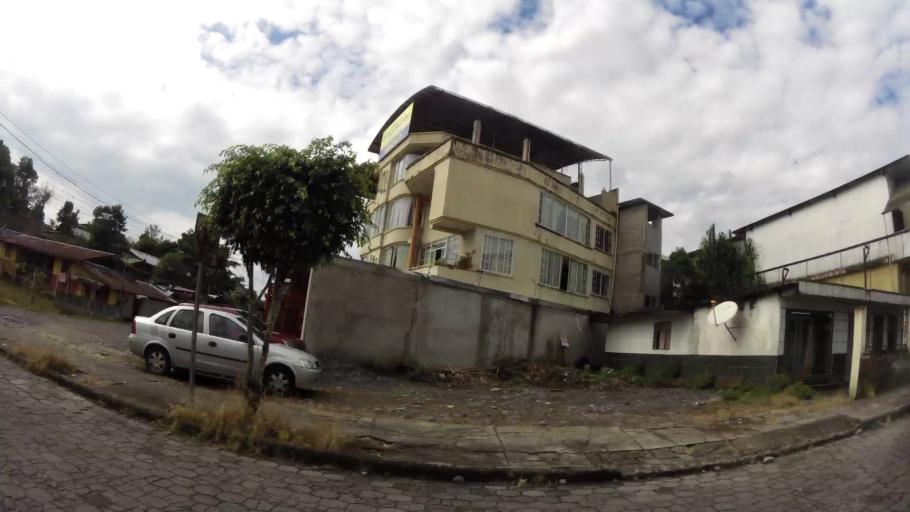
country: EC
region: Pastaza
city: Puyo
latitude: -1.4849
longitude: -78.0018
